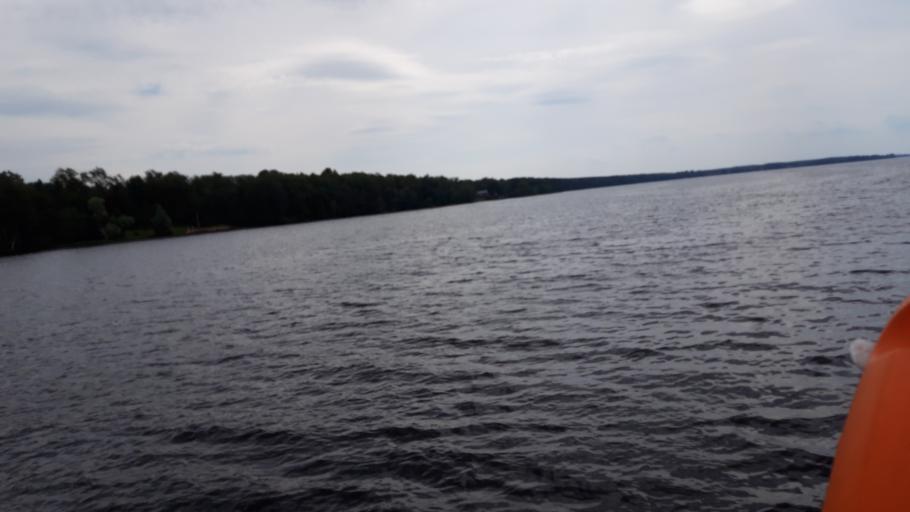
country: RU
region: Tverskaya
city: Konakovo
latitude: 56.6921
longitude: 36.6963
